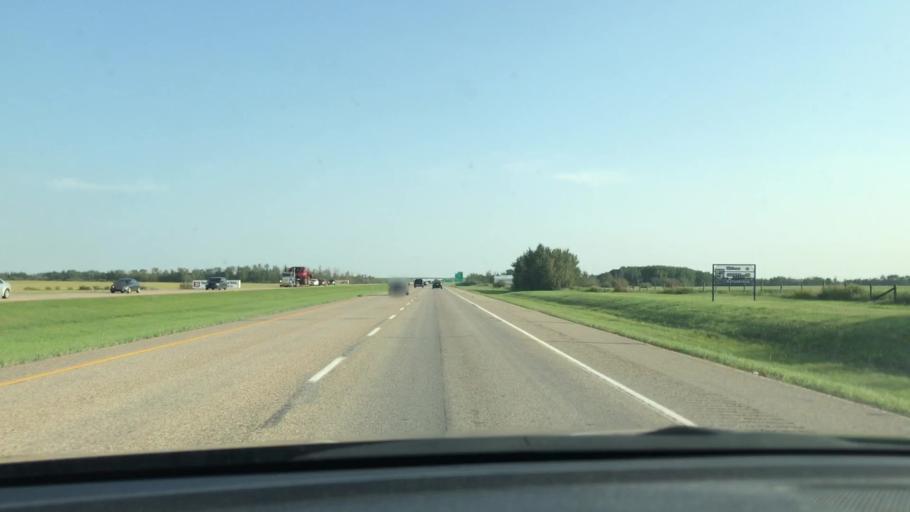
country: CA
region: Alberta
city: Millet
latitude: 53.1055
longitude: -113.5984
